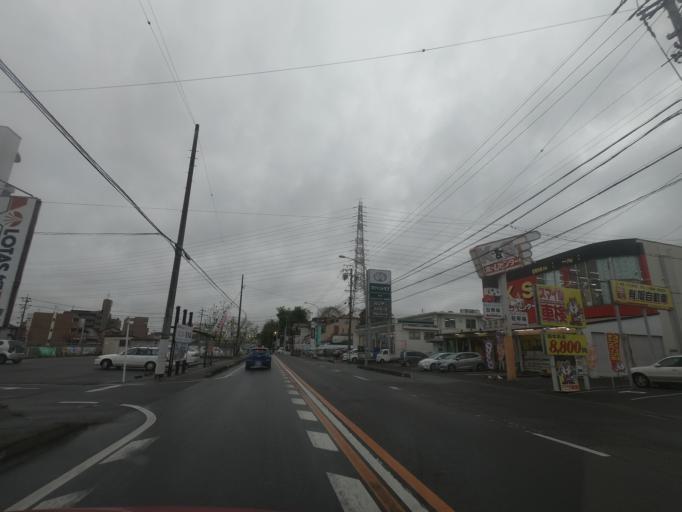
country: JP
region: Aichi
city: Kasugai
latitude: 35.2617
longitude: 137.0000
